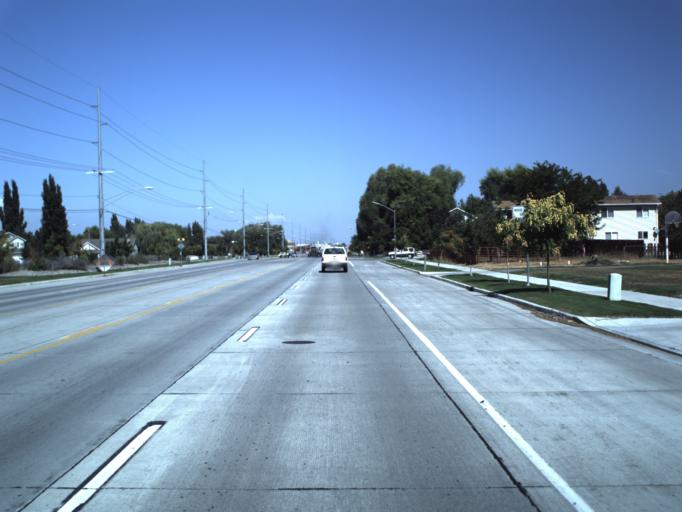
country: US
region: Utah
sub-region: Cache County
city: Logan
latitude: 41.7224
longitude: -111.8599
